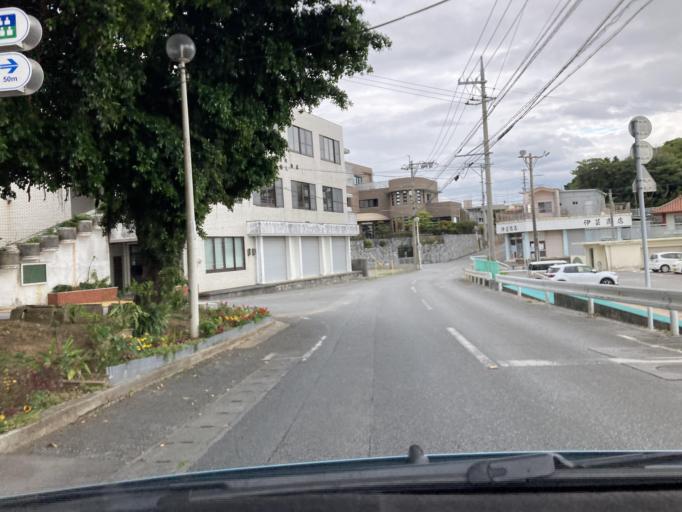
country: JP
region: Okinawa
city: Ishikawa
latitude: 26.4551
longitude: 127.9234
